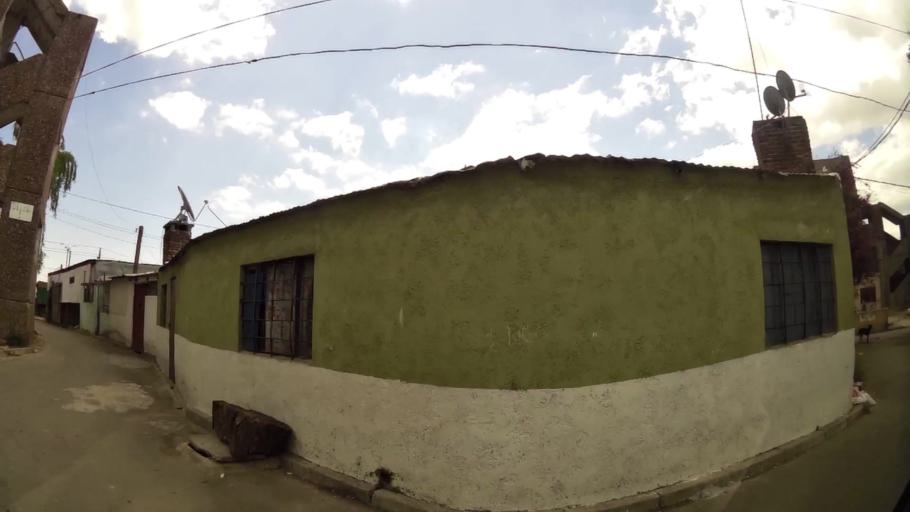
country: UY
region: Canelones
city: La Paz
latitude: -34.8211
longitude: -56.2492
